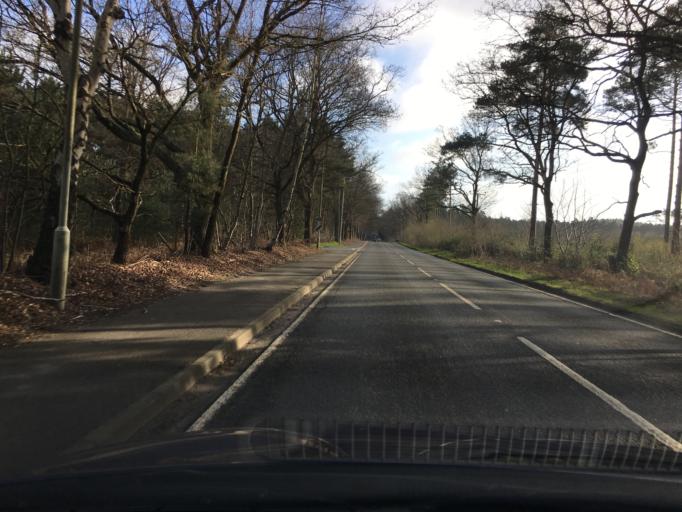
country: GB
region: England
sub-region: Bracknell Forest
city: Crowthorne
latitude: 51.3741
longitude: -0.7860
